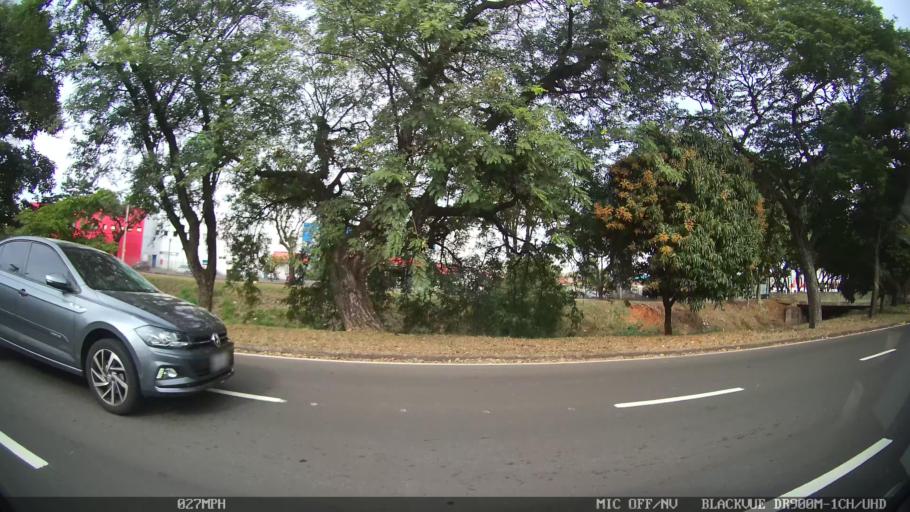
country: BR
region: Sao Paulo
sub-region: Piracicaba
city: Piracicaba
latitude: -22.7372
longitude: -47.6298
